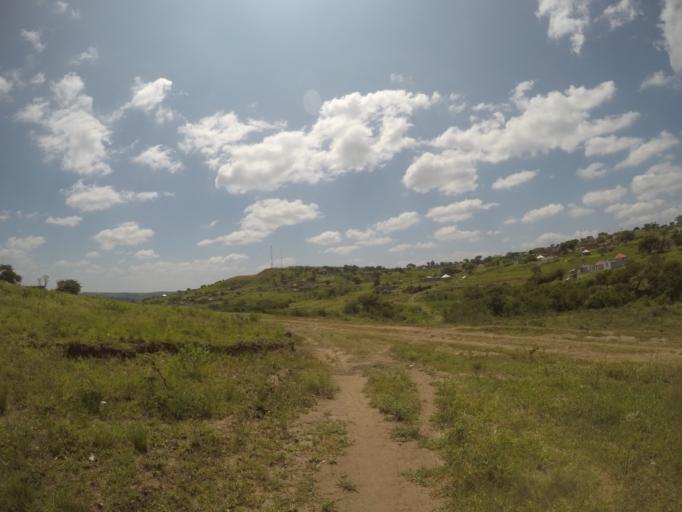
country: ZA
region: KwaZulu-Natal
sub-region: uThungulu District Municipality
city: Empangeni
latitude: -28.6038
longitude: 31.7375
